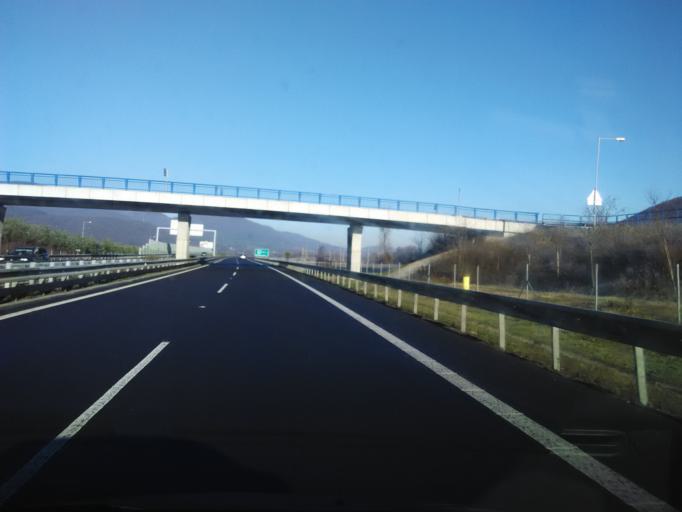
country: SK
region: Banskobystricky
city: Zarnovica
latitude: 48.5109
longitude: 18.7328
